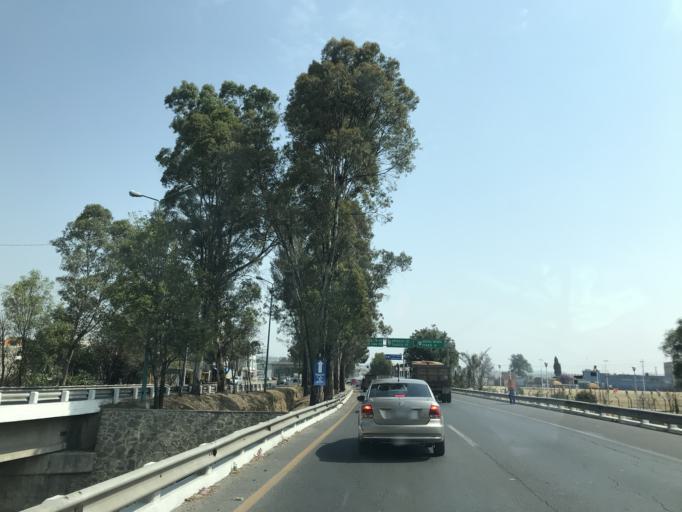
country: MX
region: Tlaxcala
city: Tlaxcala de Xicohtencatl
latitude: 19.3219
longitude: -98.2011
